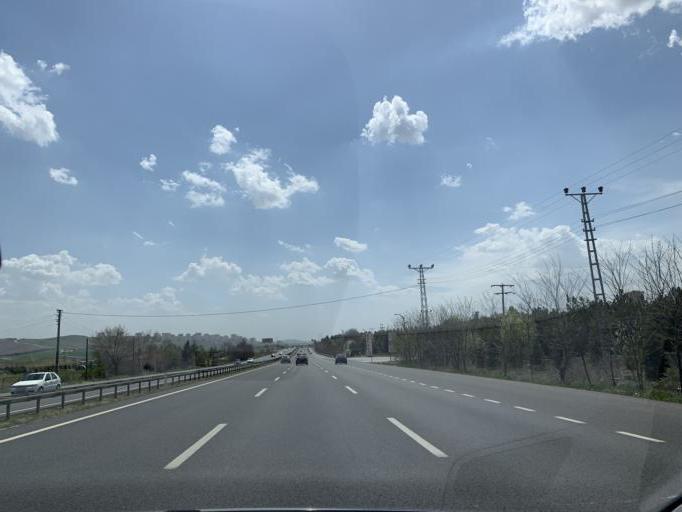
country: TR
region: Ankara
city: Etimesgut
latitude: 39.8459
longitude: 32.5952
